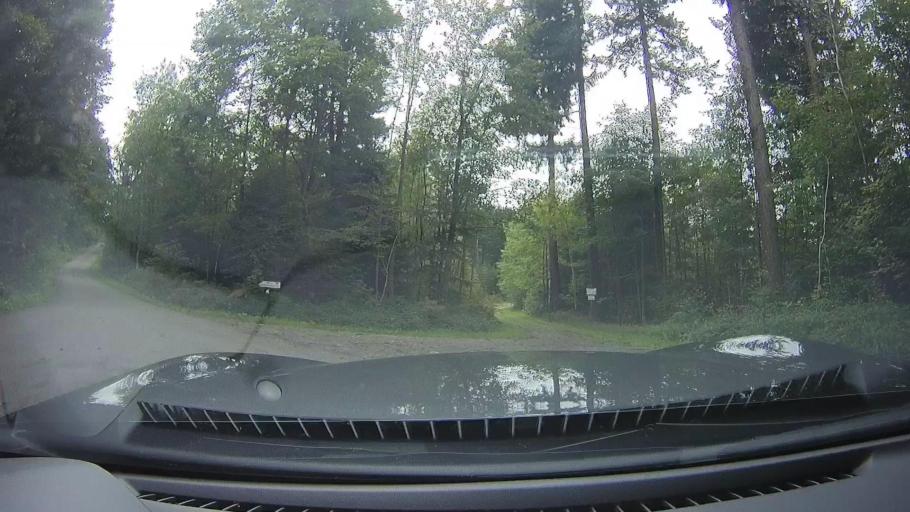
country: DE
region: Baden-Wuerttemberg
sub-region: Regierungsbezirk Stuttgart
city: Sulzbach an der Murr
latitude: 48.9798
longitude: 9.5048
